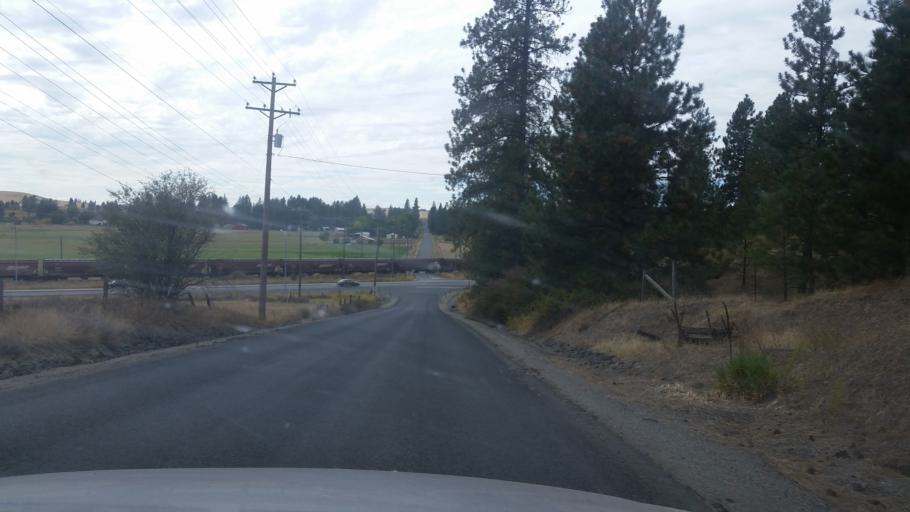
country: US
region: Washington
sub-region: Spokane County
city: Cheney
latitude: 47.5292
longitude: -117.5668
